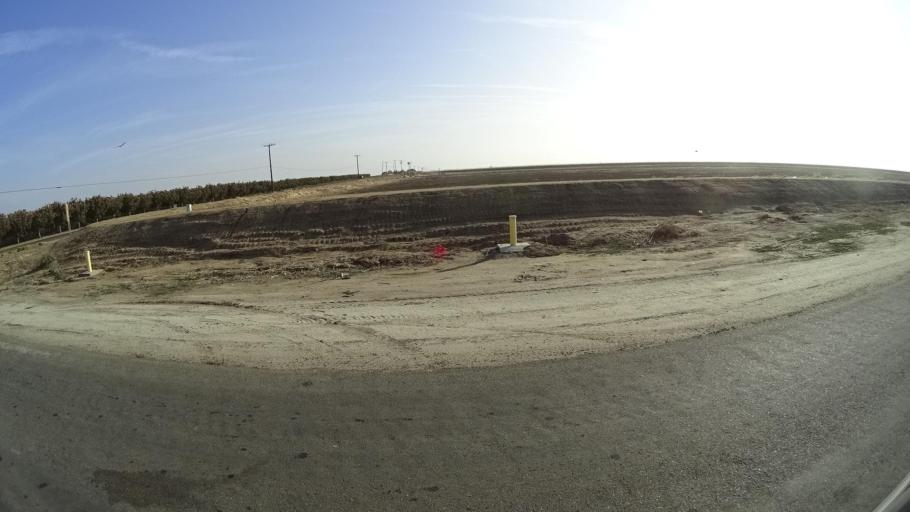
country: US
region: California
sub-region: Kern County
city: McFarland
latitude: 35.7175
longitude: -119.1872
